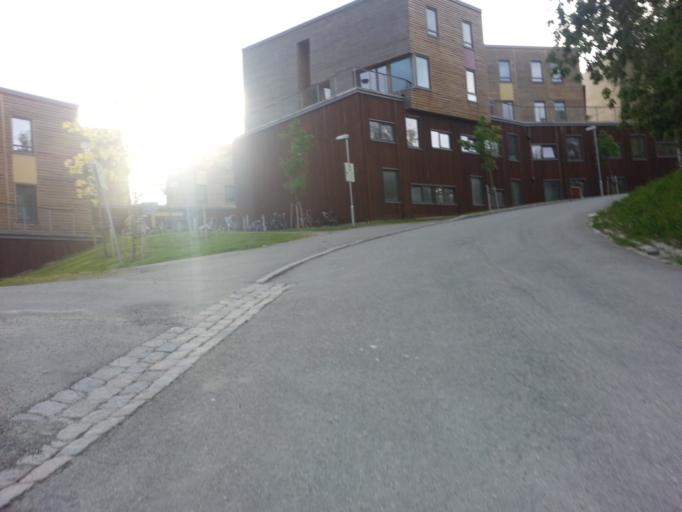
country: NO
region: Sor-Trondelag
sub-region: Trondheim
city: Trondheim
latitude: 63.4140
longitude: 10.4193
